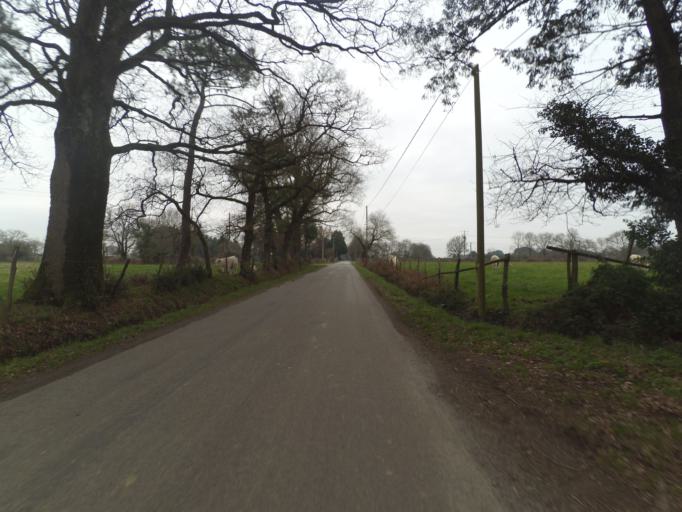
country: FR
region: Pays de la Loire
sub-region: Departement de la Loire-Atlantique
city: Sautron
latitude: 47.2565
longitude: -1.7075
